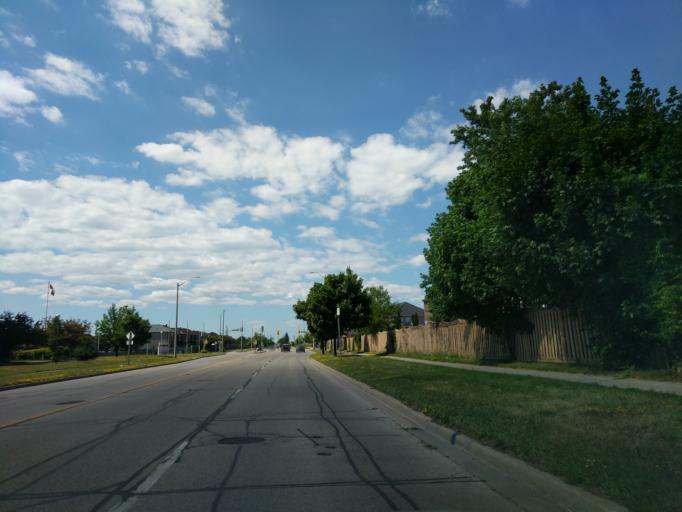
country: CA
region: Ontario
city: Markham
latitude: 43.8467
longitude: -79.2663
